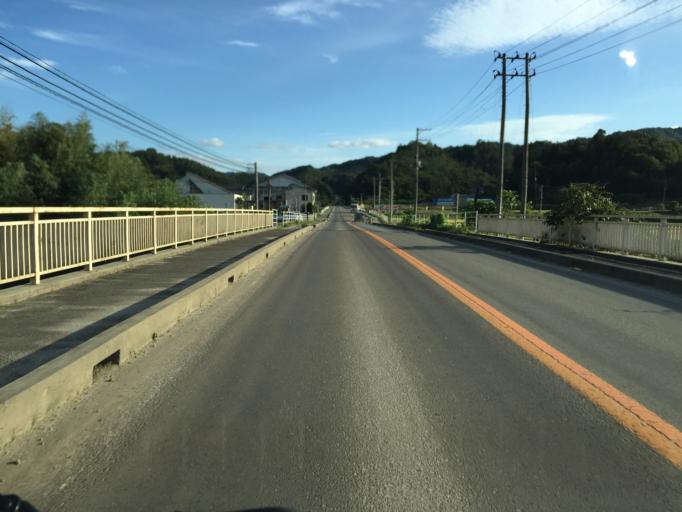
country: JP
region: Fukushima
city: Hobaramachi
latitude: 37.6996
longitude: 140.6073
